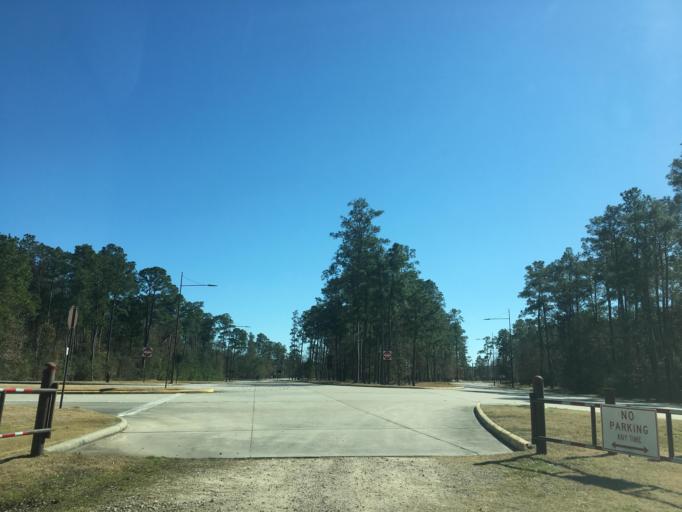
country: US
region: Texas
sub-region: Harris County
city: Spring
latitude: 30.0993
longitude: -95.4528
